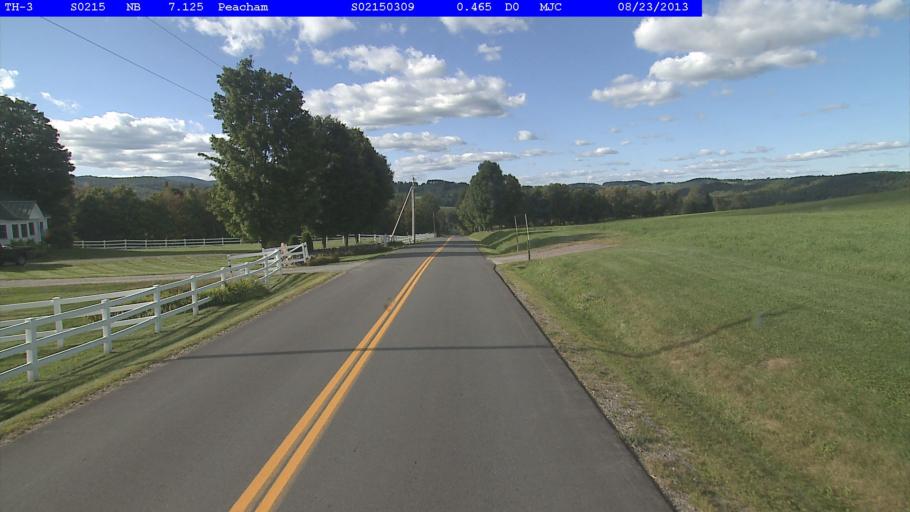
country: US
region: Vermont
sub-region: Caledonia County
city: Saint Johnsbury
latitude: 44.3045
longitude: -72.1647
